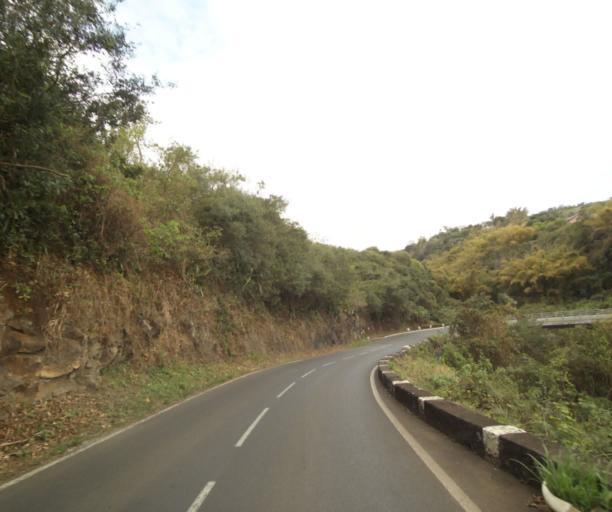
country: RE
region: Reunion
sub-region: Reunion
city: Trois-Bassins
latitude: -21.0645
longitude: 55.2808
